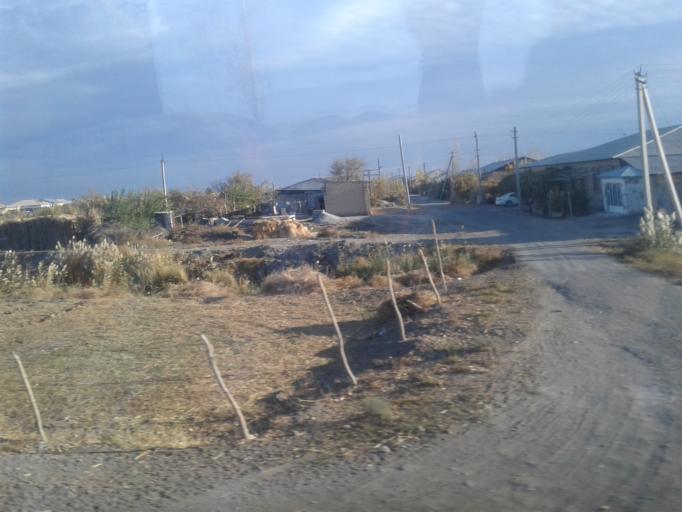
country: TM
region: Mary
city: Seydi
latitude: 39.3655
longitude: 62.9339
